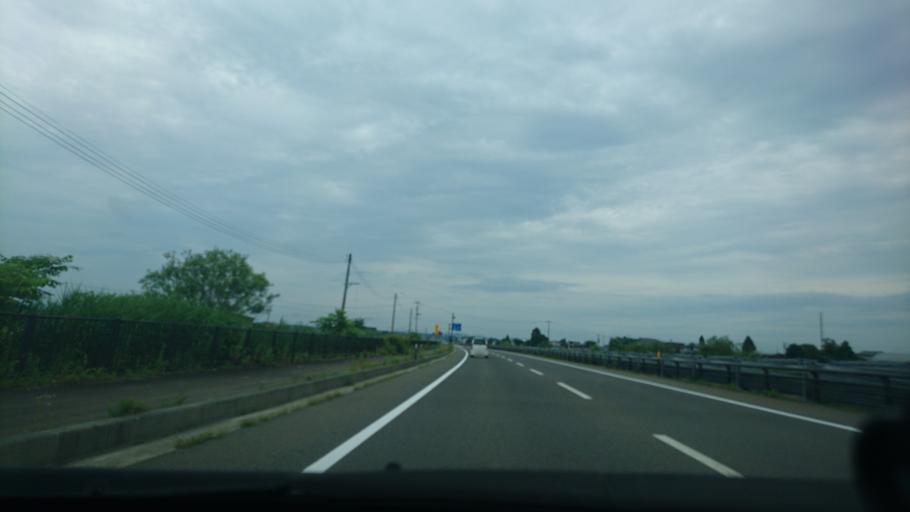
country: JP
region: Akita
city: Omagari
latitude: 39.4971
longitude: 140.4442
